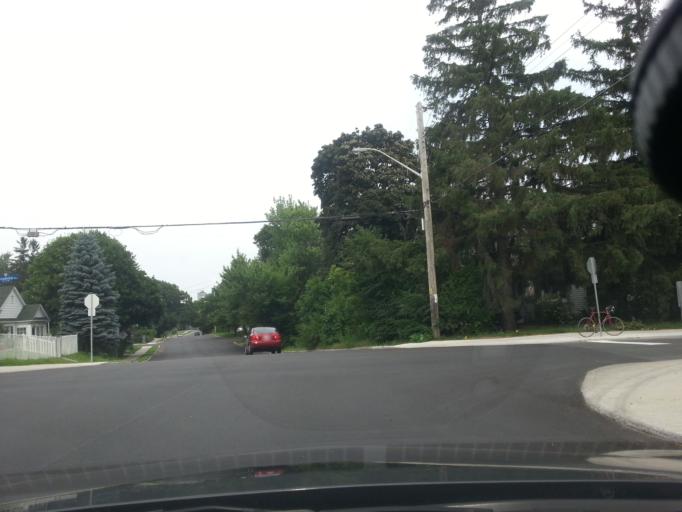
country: CA
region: Ontario
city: Ottawa
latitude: 45.3815
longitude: -75.7572
